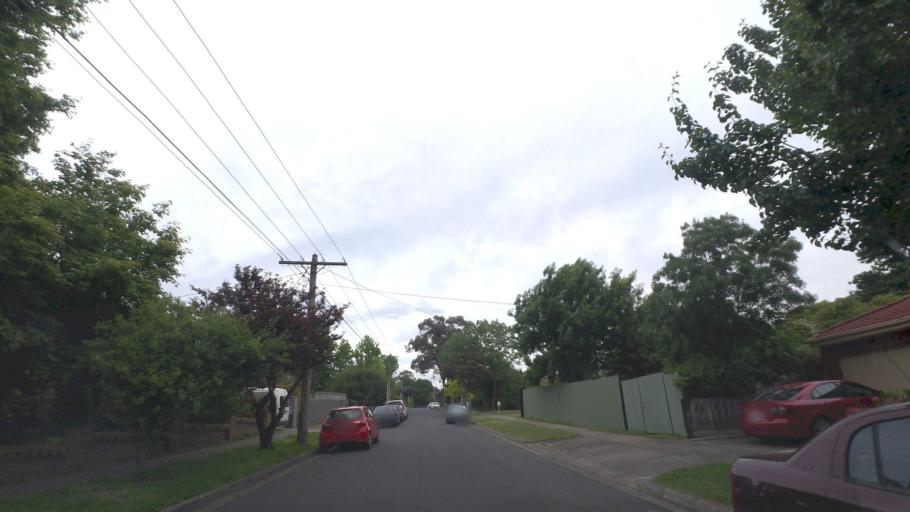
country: AU
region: Victoria
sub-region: Maroondah
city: Croydon North
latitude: -37.7913
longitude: 145.2890
